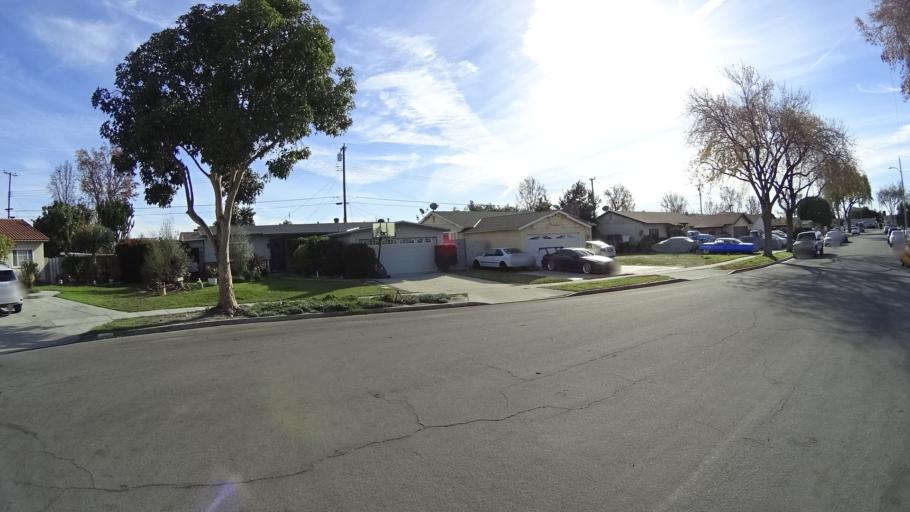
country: US
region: California
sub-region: Orange County
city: Garden Grove
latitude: 33.7577
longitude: -117.9435
